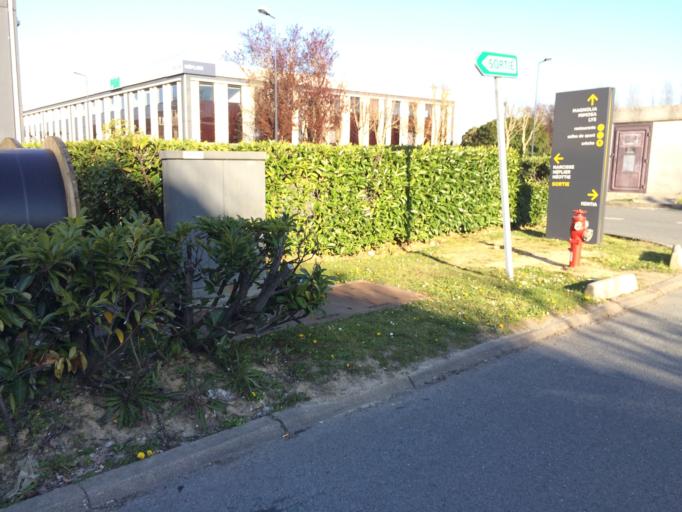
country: FR
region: Ile-de-France
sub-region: Departement de l'Essonne
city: Villejust
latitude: 48.6894
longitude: 2.2159
